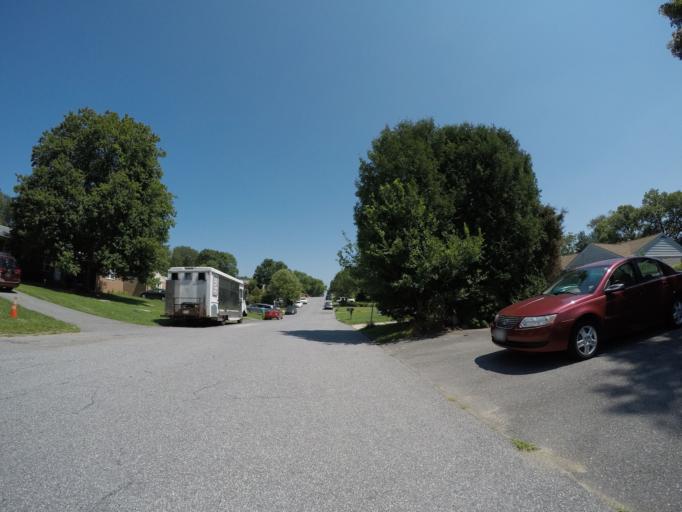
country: US
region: Maryland
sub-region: Howard County
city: Columbia
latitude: 39.2752
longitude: -76.8727
